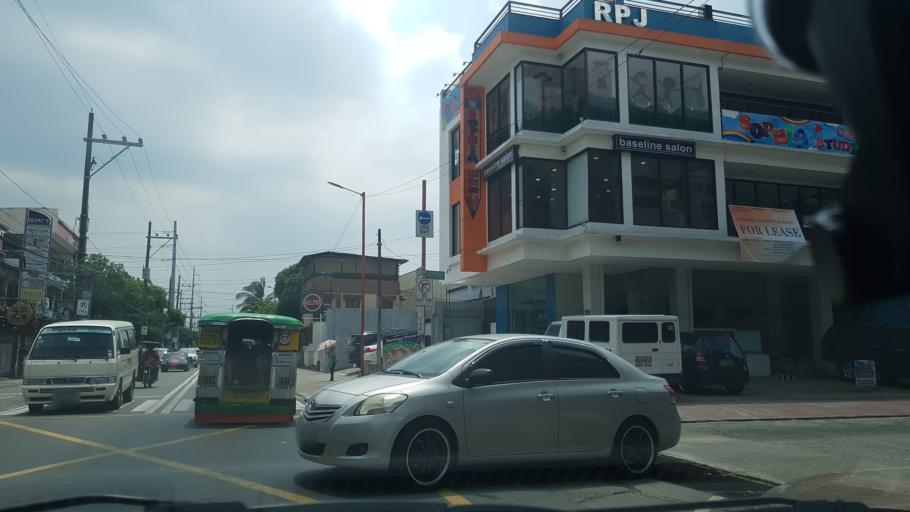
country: PH
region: Calabarzon
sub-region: Province of Rizal
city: Antipolo
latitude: 14.6397
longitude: 121.1218
